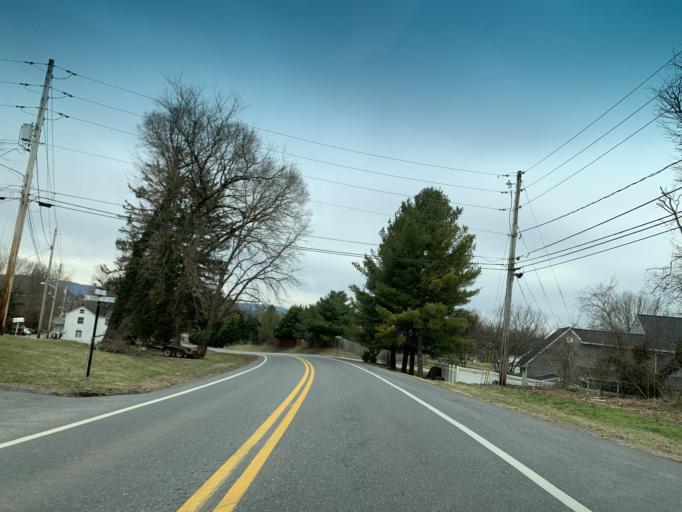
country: US
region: West Virginia
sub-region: Jefferson County
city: Charles Town
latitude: 39.2819
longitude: -77.8572
